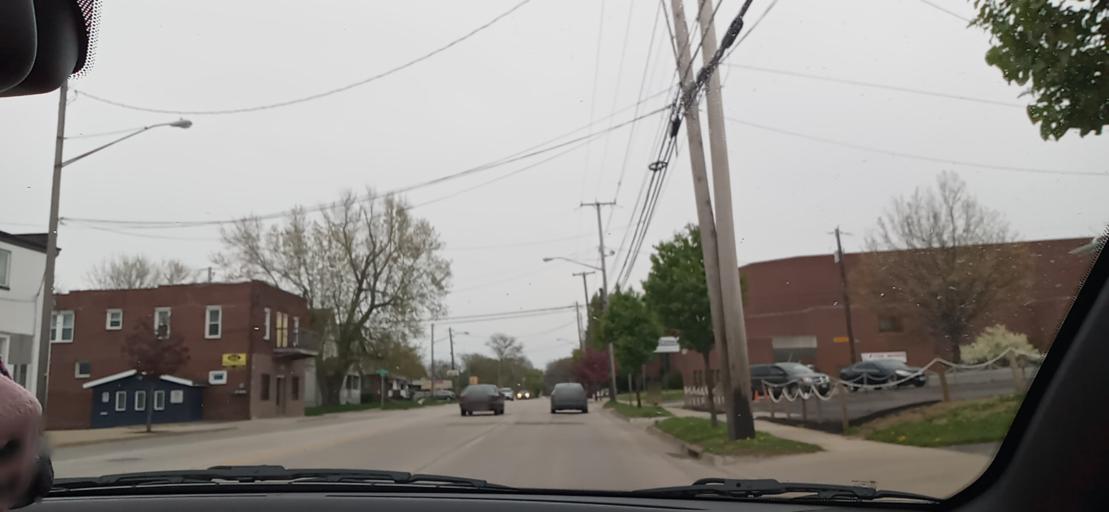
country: US
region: Ohio
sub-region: Summit County
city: Portage Lakes
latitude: 41.0372
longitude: -81.5459
